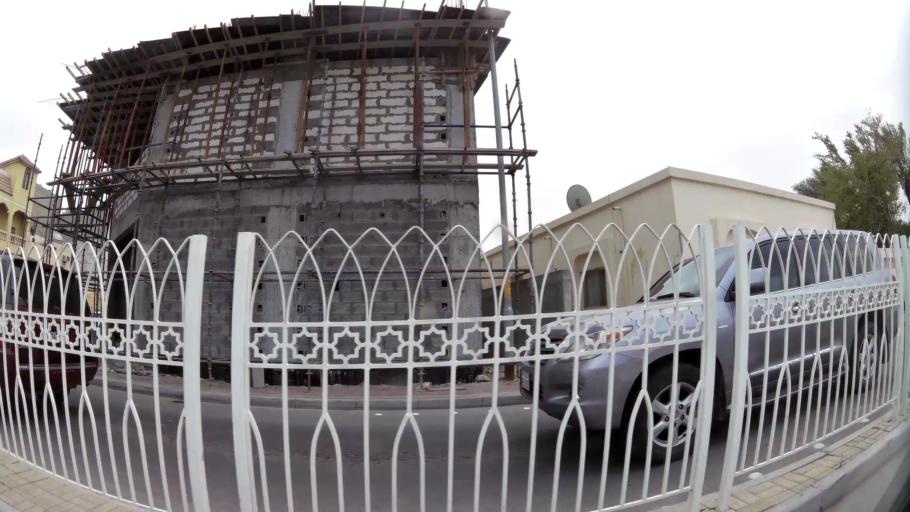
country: BH
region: Northern
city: Ar Rifa'
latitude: 26.1276
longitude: 50.5431
